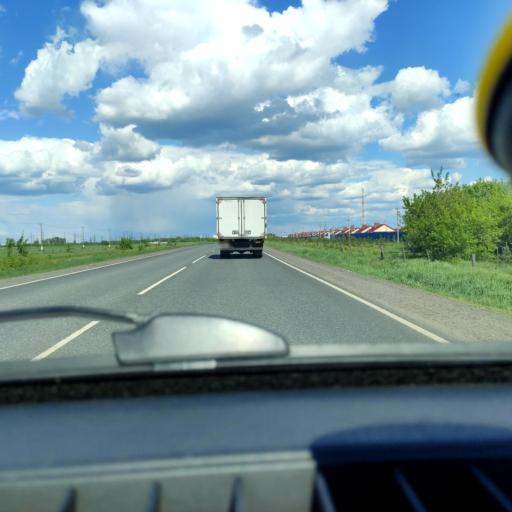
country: RU
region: Samara
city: Povolzhskiy
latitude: 53.6443
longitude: 49.6683
